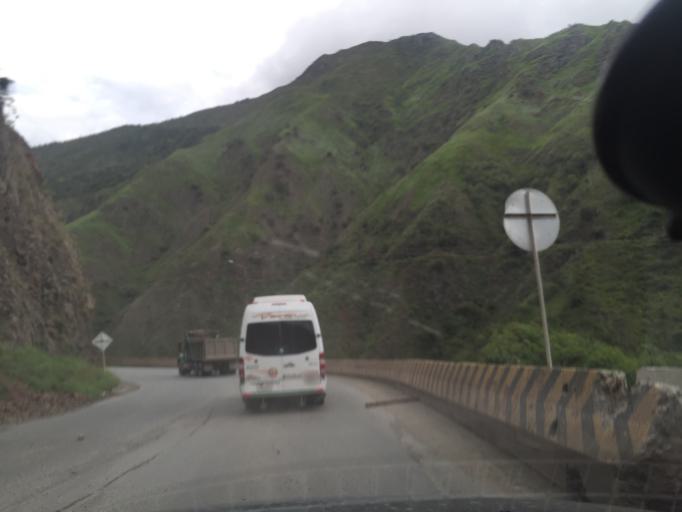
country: CO
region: Valle del Cauca
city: Dagua
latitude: 3.7747
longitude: -76.6986
